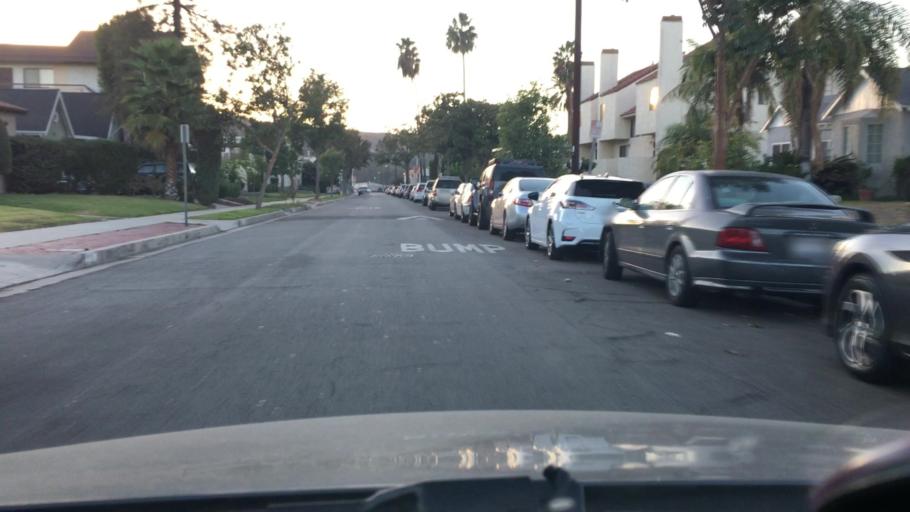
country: US
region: California
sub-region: Los Angeles County
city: Glendale
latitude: 34.1459
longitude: -118.2678
